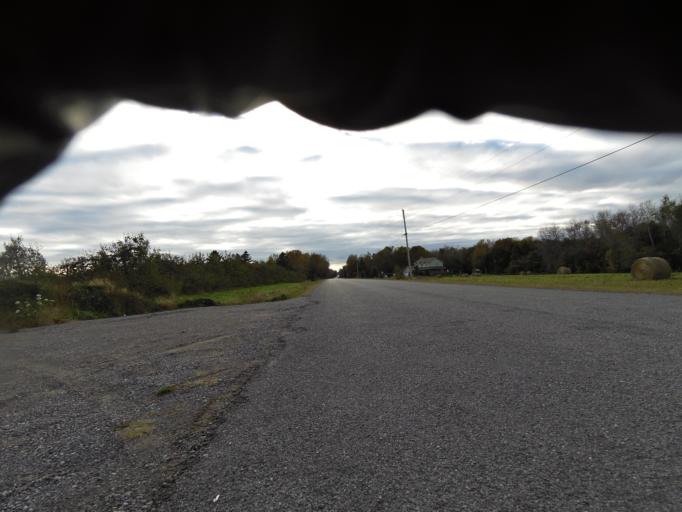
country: CA
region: Ontario
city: Cobourg
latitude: 43.9792
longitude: -77.9934
